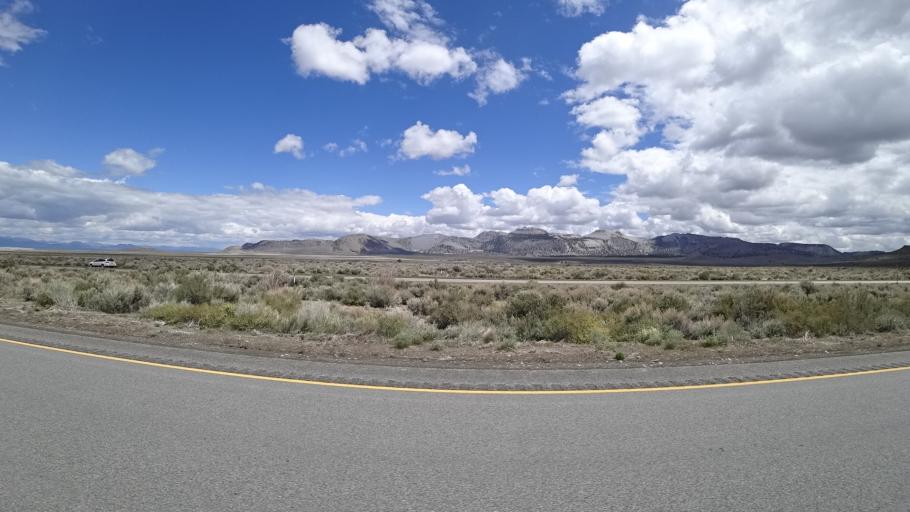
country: US
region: California
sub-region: Mono County
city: Mammoth Lakes
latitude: 37.8780
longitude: -119.0897
